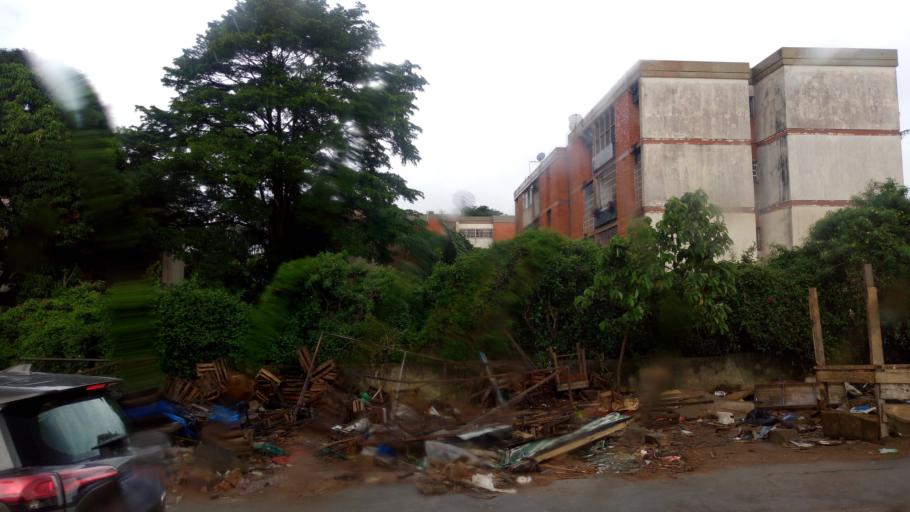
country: CI
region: Lagunes
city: Abobo
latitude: 5.3658
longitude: -3.9897
